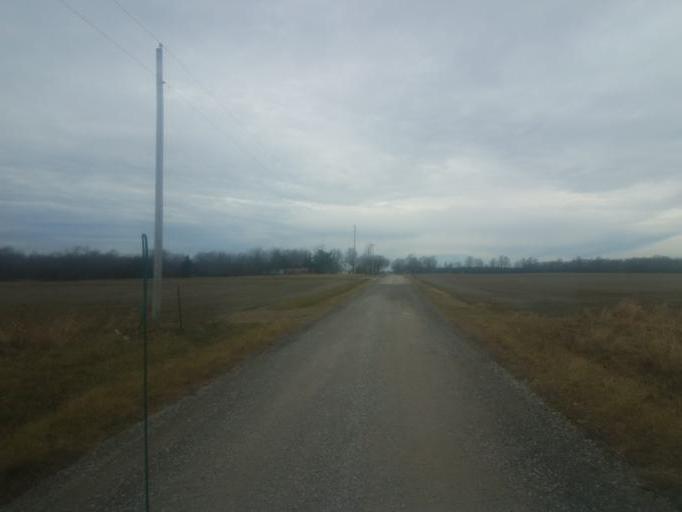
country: US
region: Ohio
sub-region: Morrow County
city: Mount Gilead
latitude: 40.6235
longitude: -82.9042
